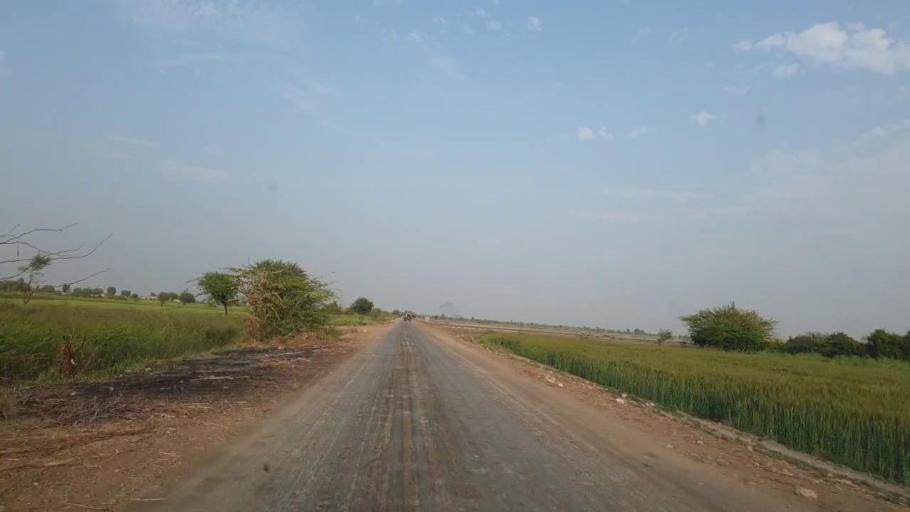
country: PK
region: Sindh
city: Pithoro
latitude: 25.5708
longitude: 69.2450
